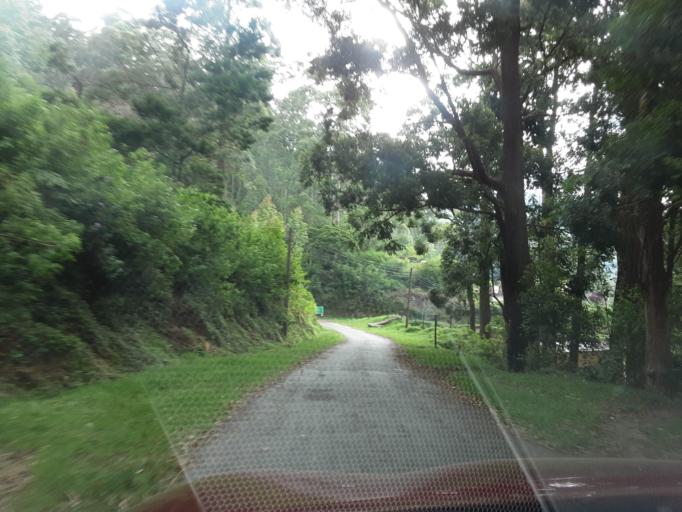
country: LK
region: Uva
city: Haputale
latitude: 6.8165
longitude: 80.8449
